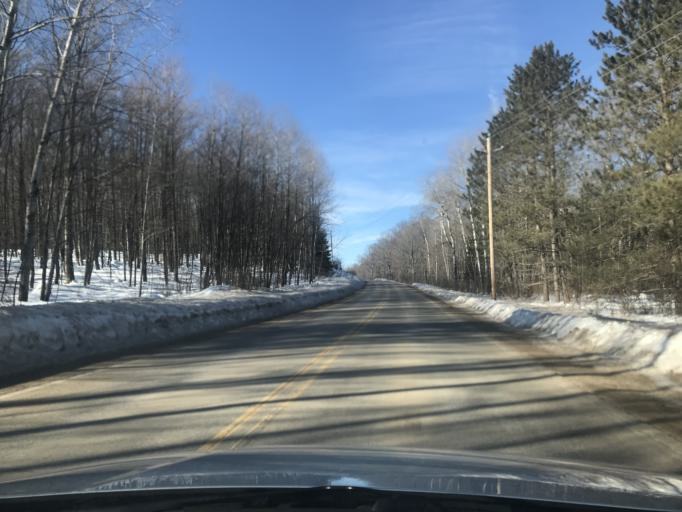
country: US
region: Michigan
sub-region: Dickinson County
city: Kingsford
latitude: 45.4191
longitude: -88.4066
